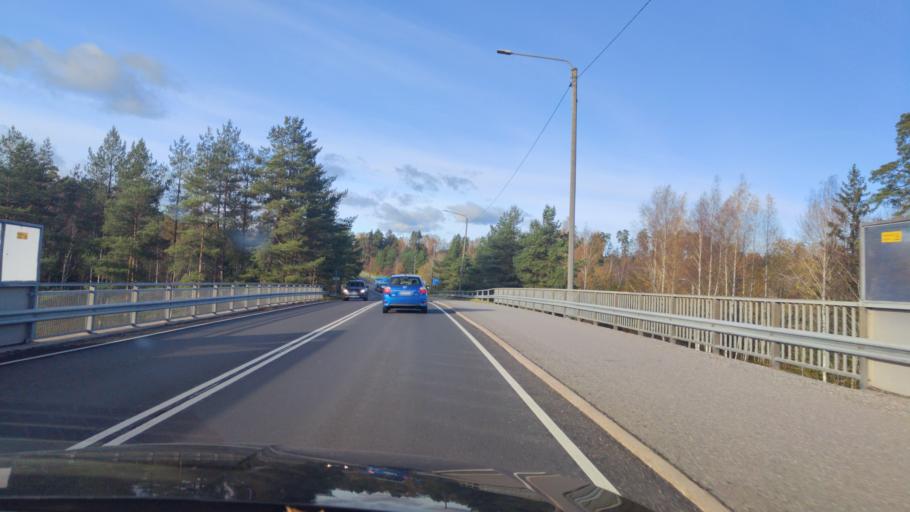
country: FI
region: Varsinais-Suomi
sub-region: Turku
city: Kaarina
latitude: 60.4422
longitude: 22.3814
